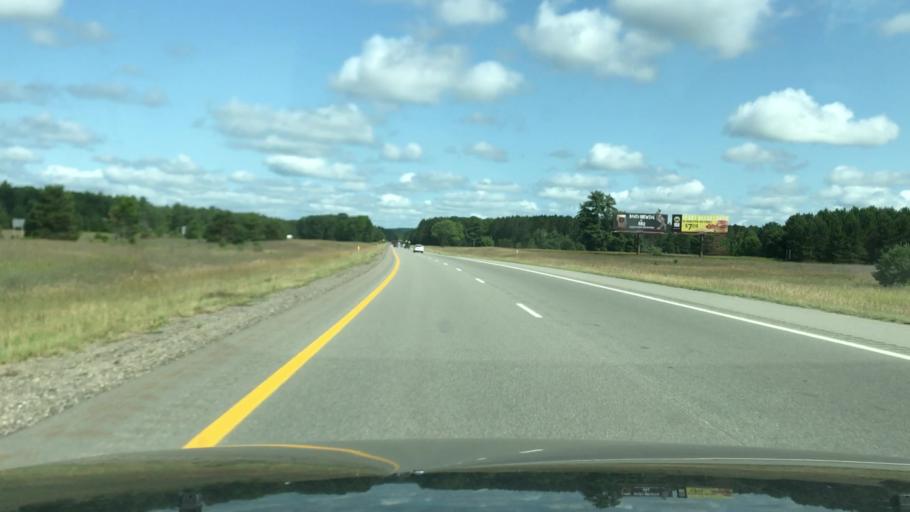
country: US
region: Michigan
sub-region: Mecosta County
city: Big Rapids
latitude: 43.5997
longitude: -85.4883
